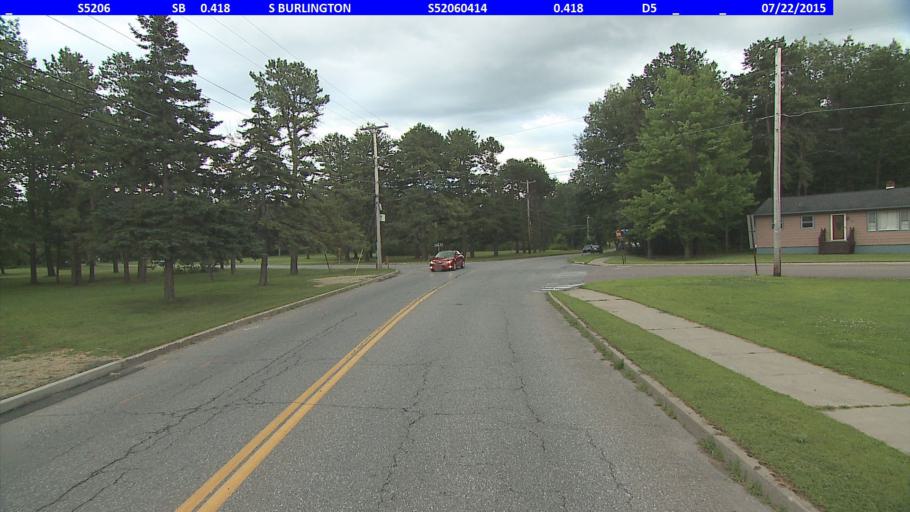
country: US
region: Vermont
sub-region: Chittenden County
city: South Burlington
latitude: 44.4764
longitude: -73.1659
